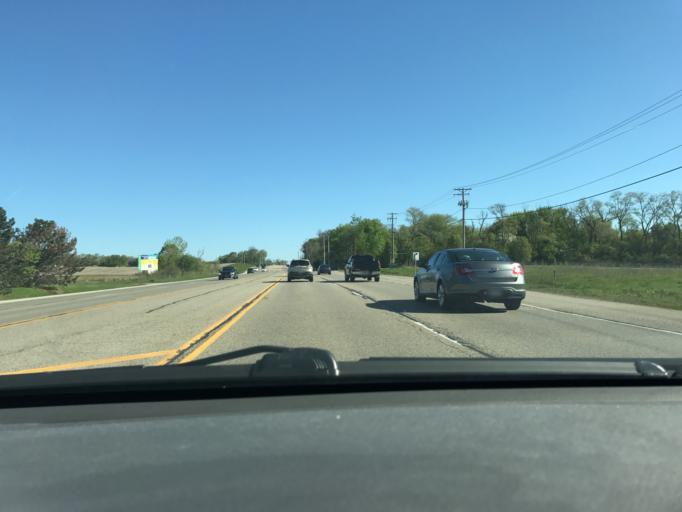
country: US
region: Illinois
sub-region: Kane County
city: Sleepy Hollow
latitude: 42.0981
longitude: -88.3351
